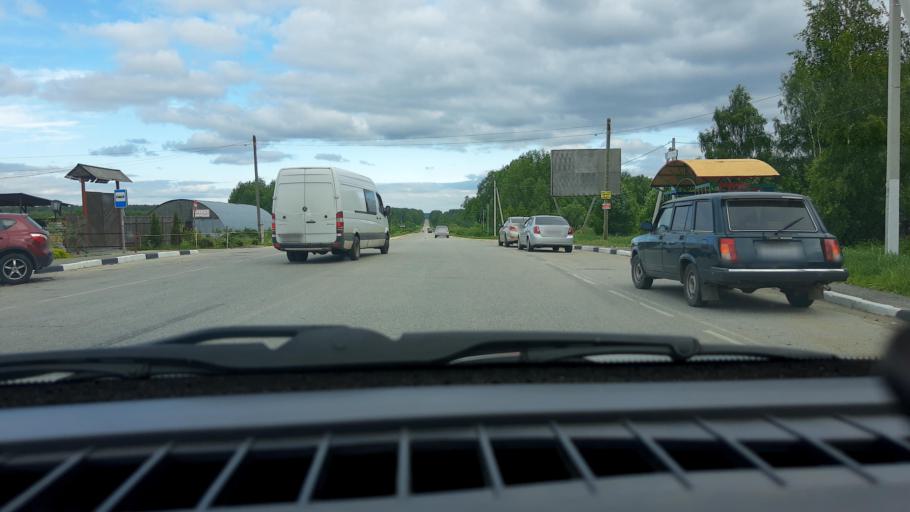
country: RU
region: Nizjnij Novgorod
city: Vladimirskoye
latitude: 56.8998
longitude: 45.0152
